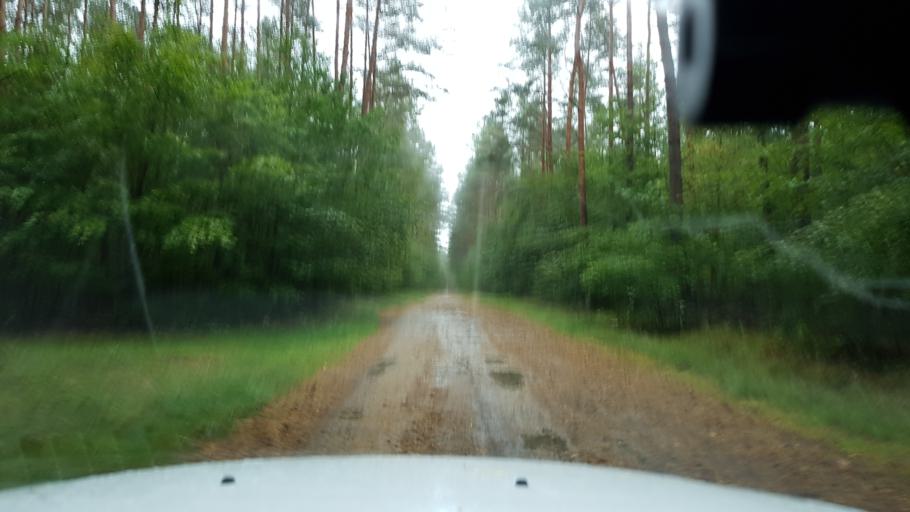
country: PL
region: West Pomeranian Voivodeship
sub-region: Powiat goleniowski
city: Przybiernow
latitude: 53.7346
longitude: 14.8029
